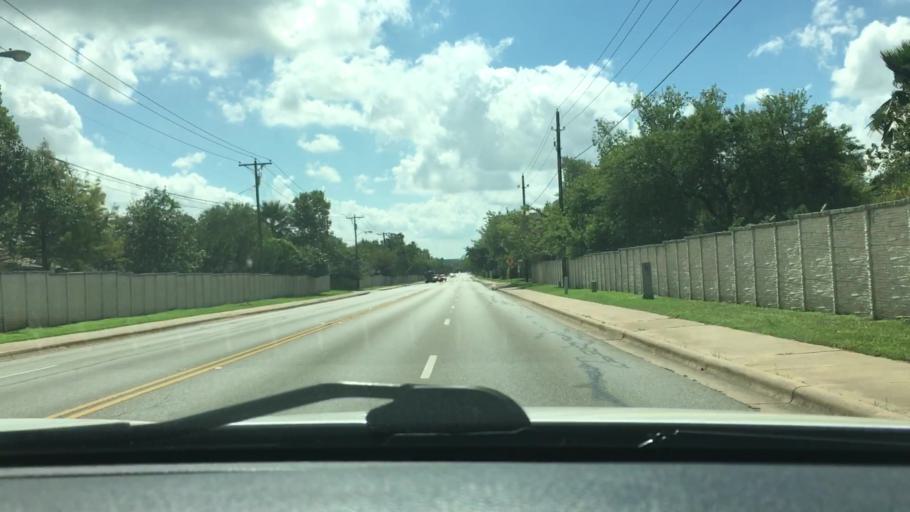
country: US
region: Texas
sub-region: Williamson County
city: Round Rock
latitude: 30.5272
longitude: -97.6679
